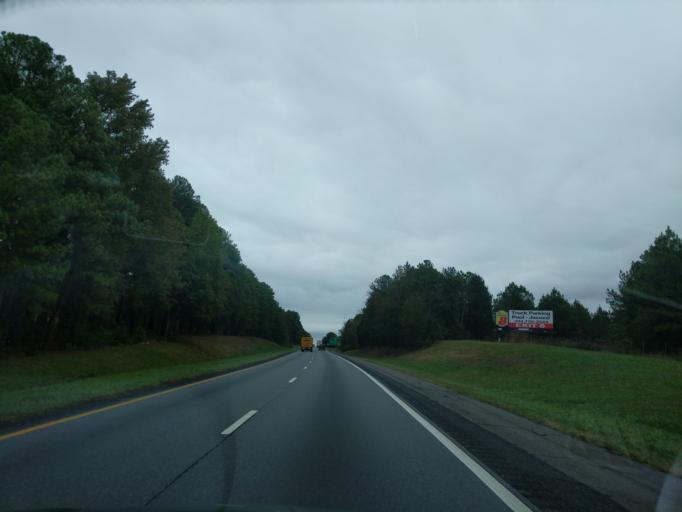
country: US
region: North Carolina
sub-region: Cleveland County
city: White Plains
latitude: 35.1732
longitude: -81.4212
